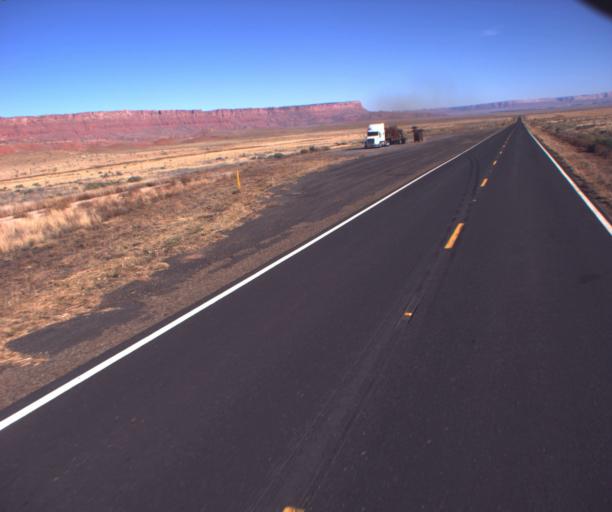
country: US
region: Arizona
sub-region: Coconino County
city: Fredonia
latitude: 36.7294
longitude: -112.0401
